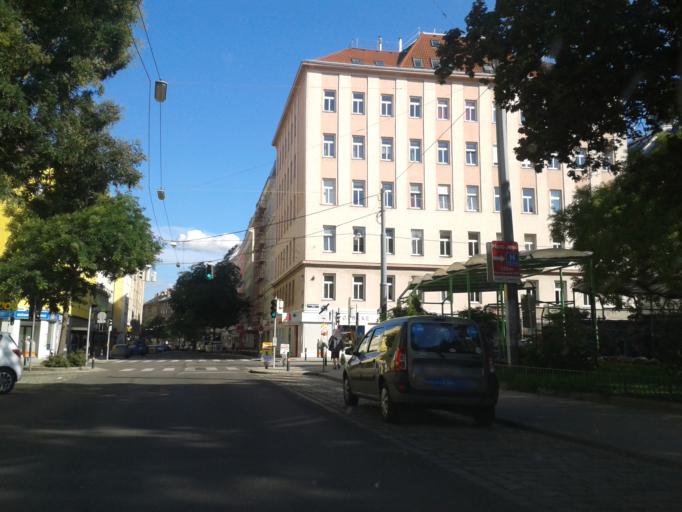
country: AT
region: Vienna
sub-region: Wien Stadt
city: Vienna
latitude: 48.1977
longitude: 16.4019
